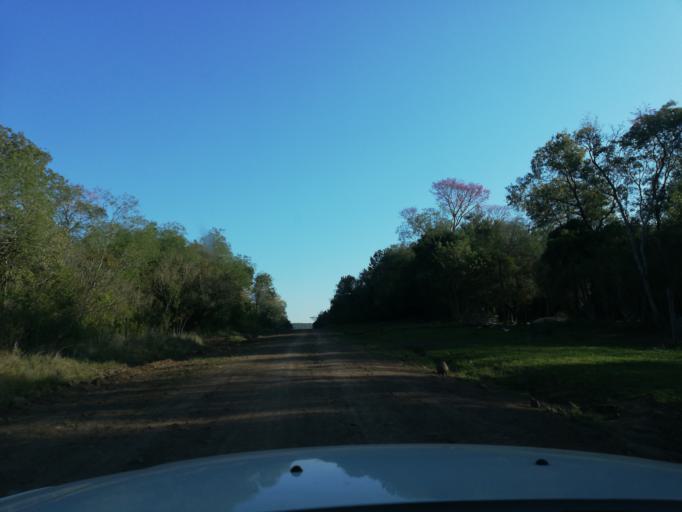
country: AR
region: Misiones
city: Cerro Cora
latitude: -27.5945
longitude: -55.6949
